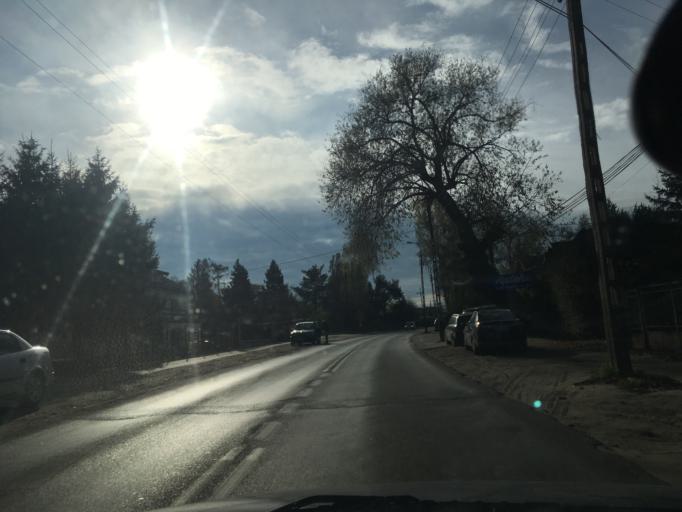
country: PL
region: Masovian Voivodeship
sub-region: Powiat piaseczynski
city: Piaseczno
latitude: 52.0560
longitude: 21.0079
